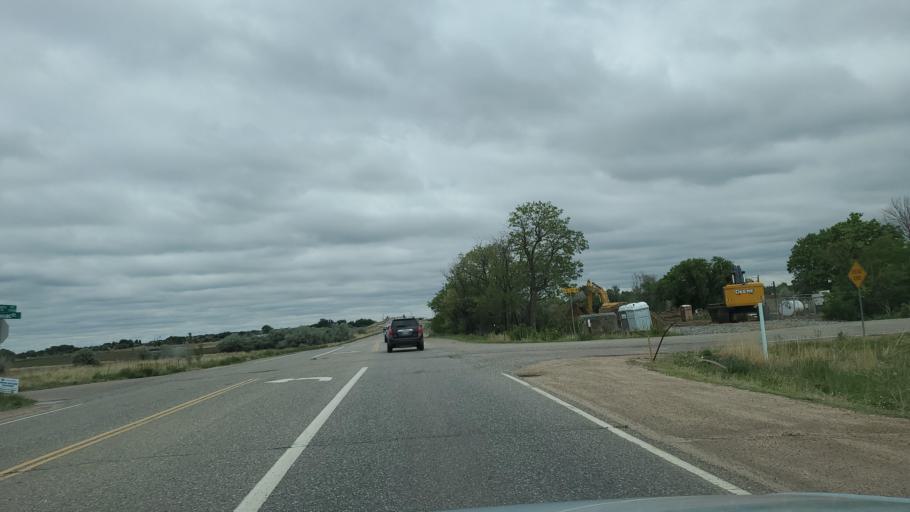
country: US
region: Colorado
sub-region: Adams County
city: Brighton
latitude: 39.9143
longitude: -104.8283
